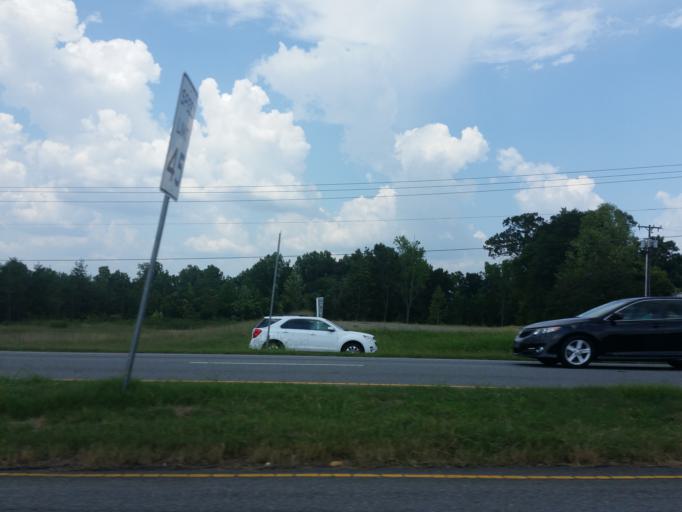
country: US
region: North Carolina
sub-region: Cleveland County
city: Shelby
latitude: 35.2731
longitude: -81.5205
